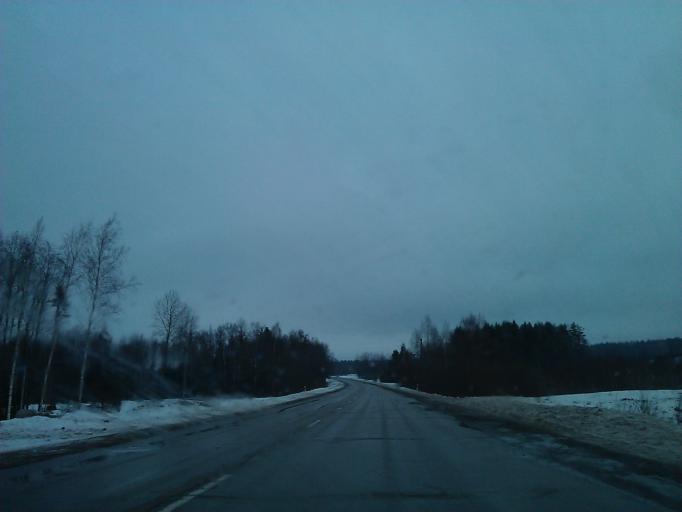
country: LV
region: Cesu Rajons
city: Cesis
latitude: 57.2874
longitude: 25.2988
